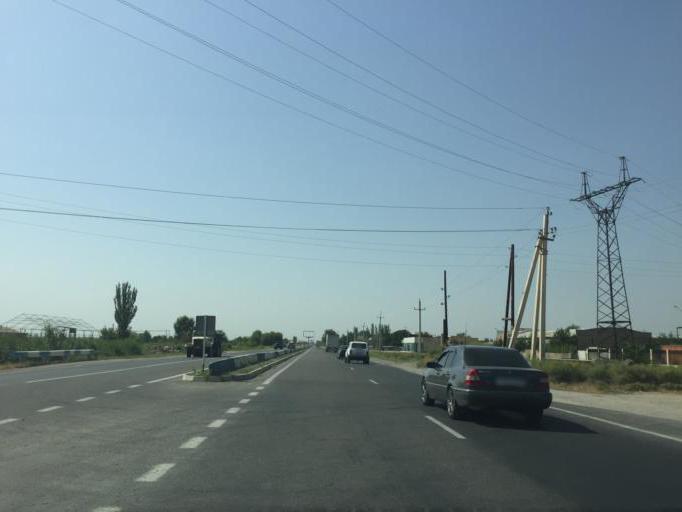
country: AM
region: Ararat
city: Shahumyan
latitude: 39.9406
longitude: 44.5563
